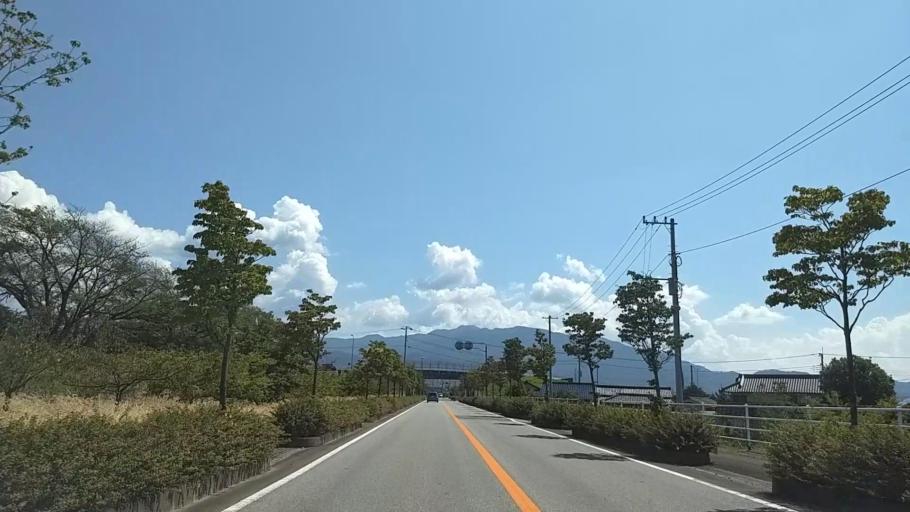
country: JP
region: Yamanashi
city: Ryuo
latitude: 35.6159
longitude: 138.5011
